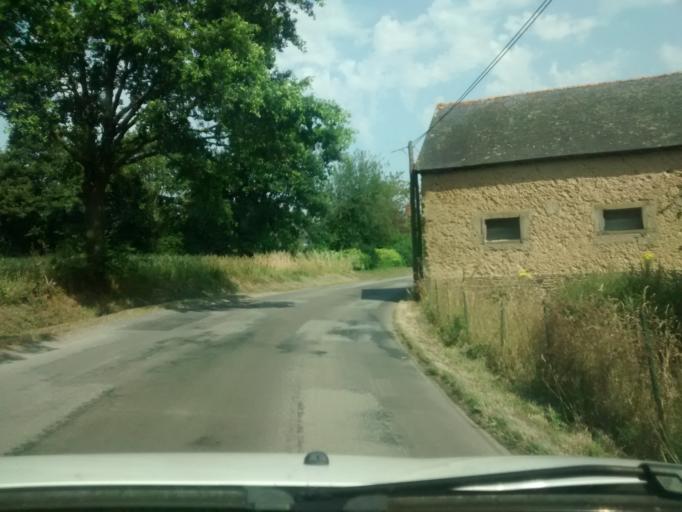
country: FR
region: Brittany
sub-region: Departement d'Ille-et-Vilaine
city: Cesson-Sevigne
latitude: 48.1427
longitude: -1.6063
